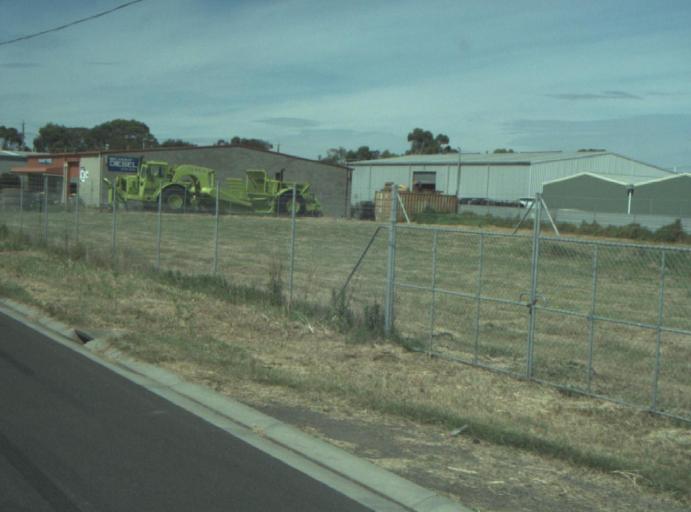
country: AU
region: Victoria
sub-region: Greater Geelong
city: East Geelong
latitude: -38.1676
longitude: 144.4110
